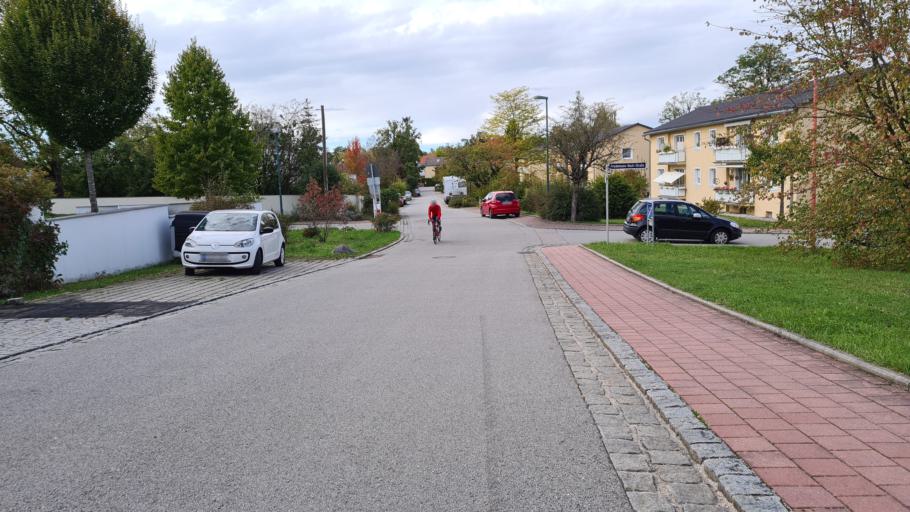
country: DE
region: Bavaria
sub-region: Upper Bavaria
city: Grafelfing
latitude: 48.1111
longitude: 11.4386
